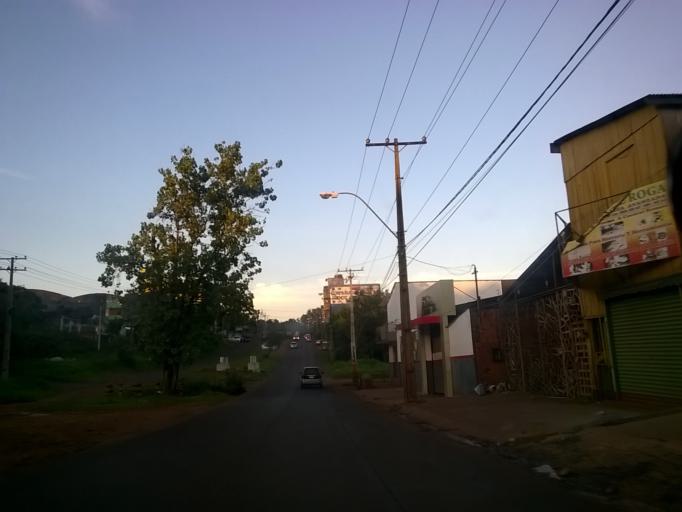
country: PY
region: Alto Parana
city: Ciudad del Este
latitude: -25.5048
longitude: -54.6537
